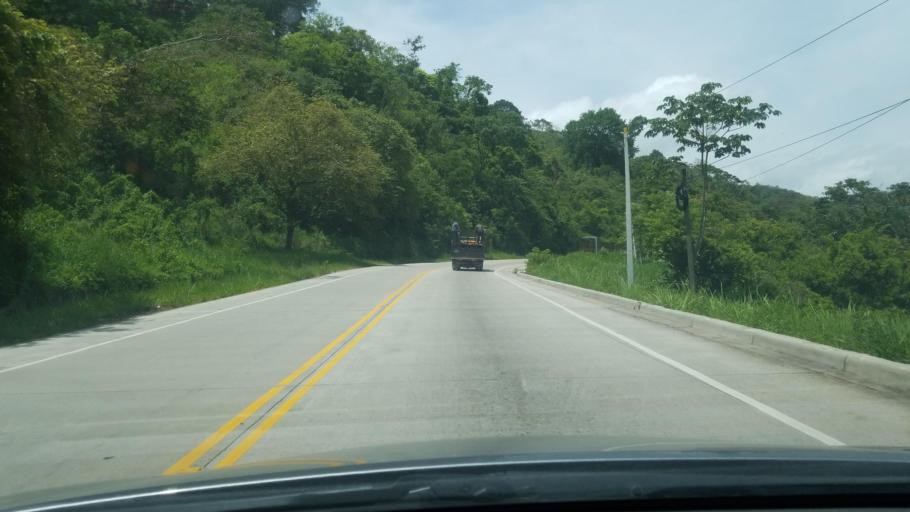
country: HN
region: Copan
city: Agua Caliente
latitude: 14.8654
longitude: -88.7872
